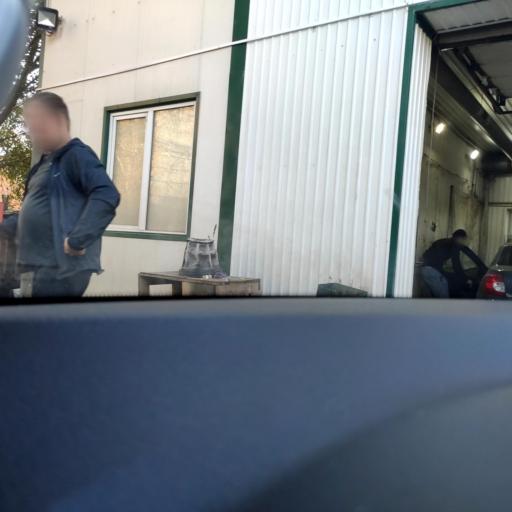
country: RU
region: Samara
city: Petra-Dubrava
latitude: 53.2489
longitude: 50.2687
